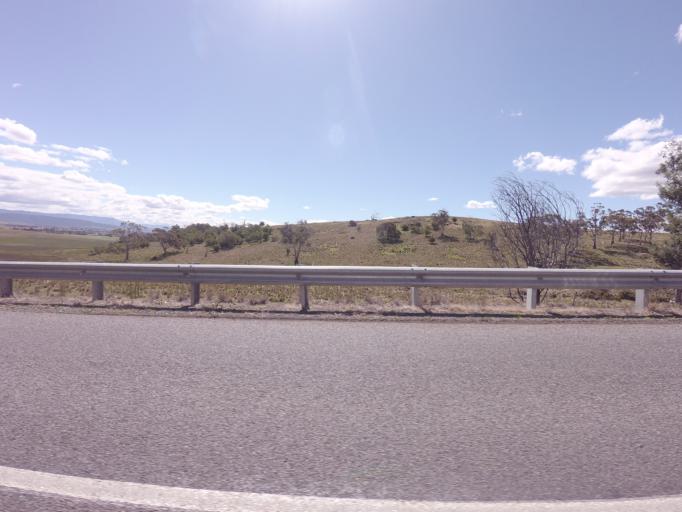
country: AU
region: Tasmania
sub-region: Northern Midlands
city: Evandale
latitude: -41.9363
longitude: 147.5730
